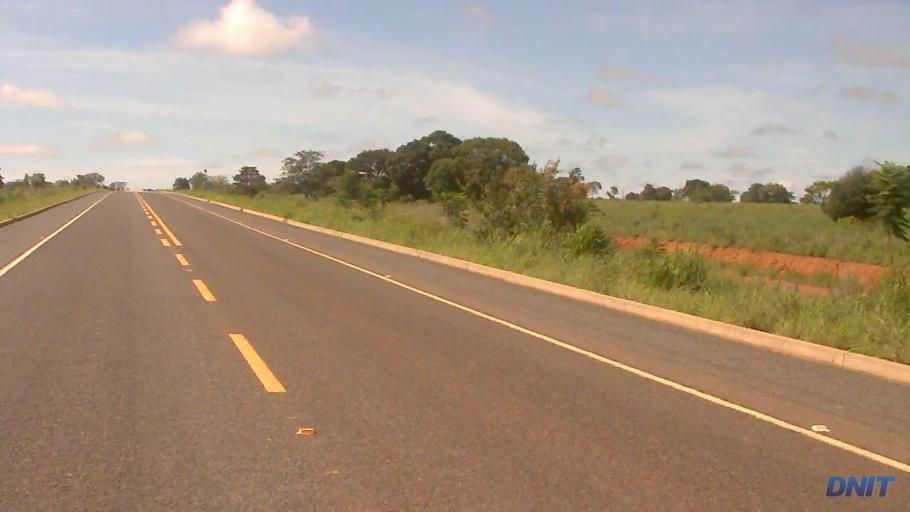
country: BR
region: Goias
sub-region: Sao Miguel Do Araguaia
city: Sao Miguel do Araguaia
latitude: -13.2995
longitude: -50.1754
